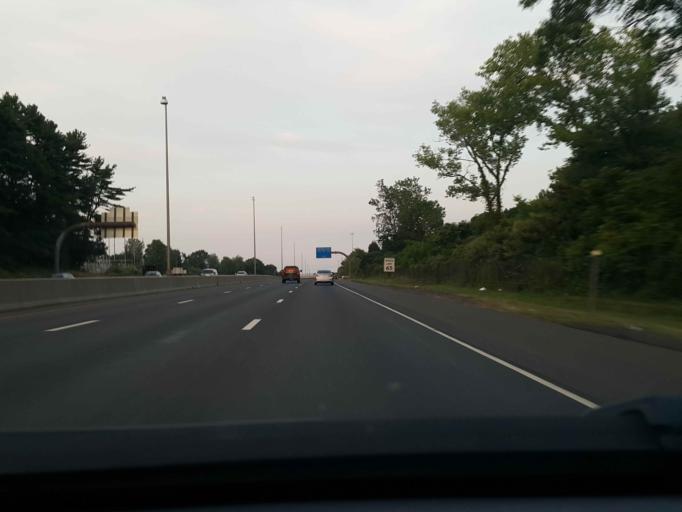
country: US
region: Connecticut
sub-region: New Haven County
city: East Haven
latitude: 41.2825
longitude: -72.8575
